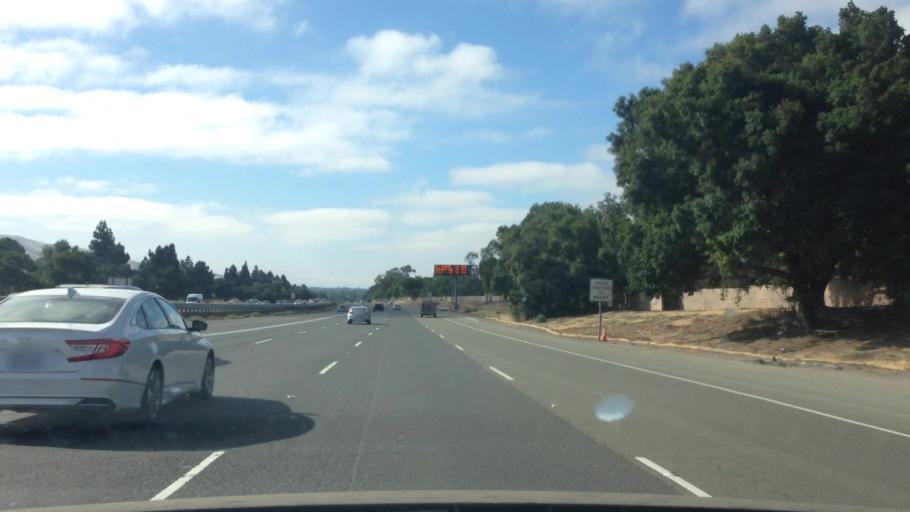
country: US
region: California
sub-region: Santa Clara County
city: Milpitas
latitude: 37.4631
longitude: -121.9033
